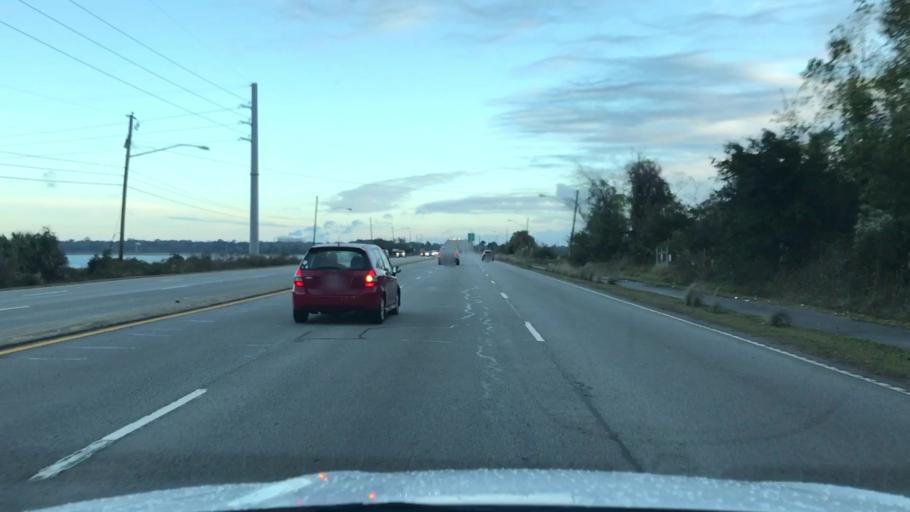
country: US
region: South Carolina
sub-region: Charleston County
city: North Charleston
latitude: 32.8303
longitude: -79.9887
